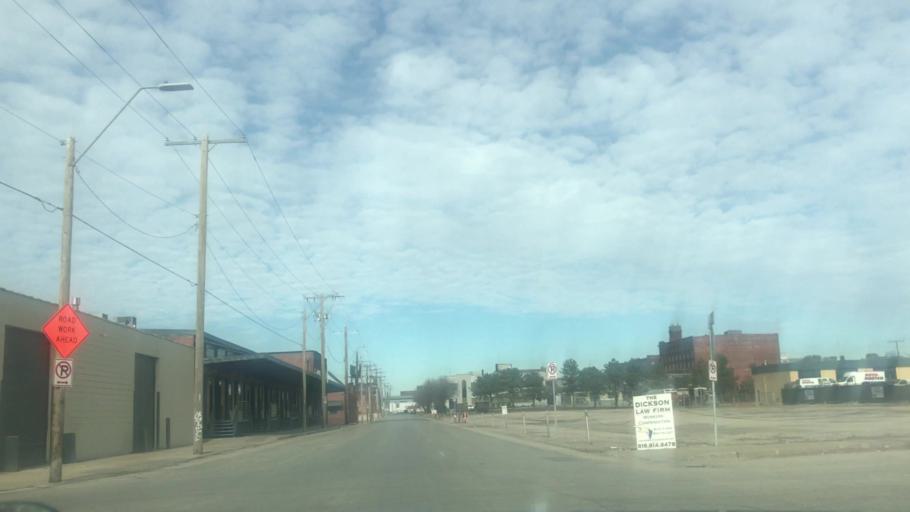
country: US
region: Missouri
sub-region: Jackson County
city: Kansas City
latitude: 39.0946
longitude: -94.6038
